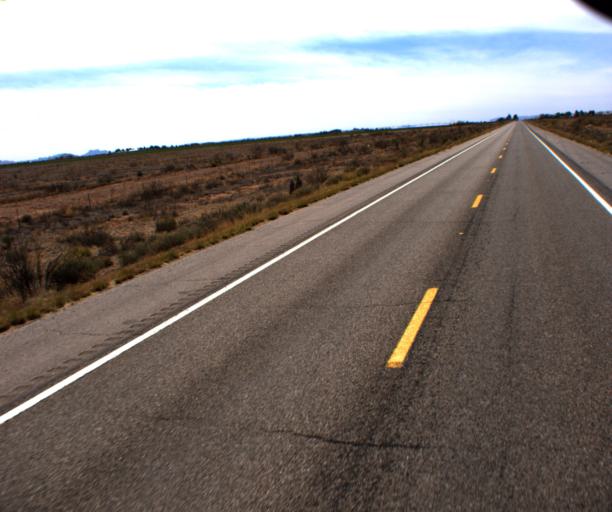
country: US
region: Arizona
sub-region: Cochise County
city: Pirtleville
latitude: 31.6162
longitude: -109.6709
